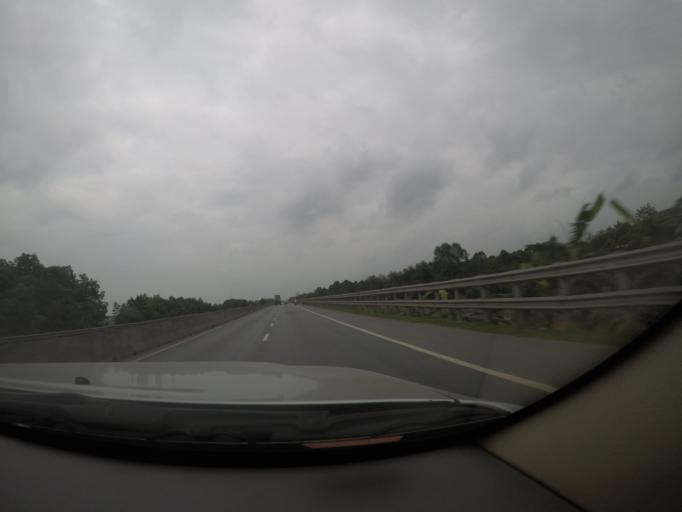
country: VN
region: Quang Tri
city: Hai Lang
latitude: 16.6511
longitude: 107.2852
